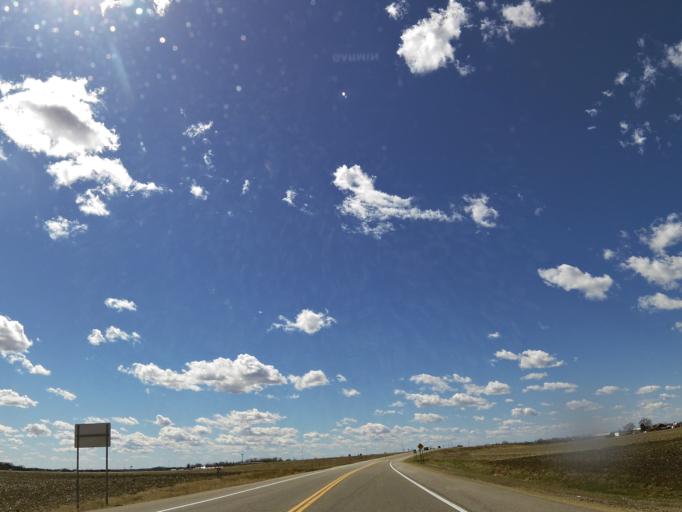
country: US
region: Minnesota
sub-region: Dakota County
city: Rosemount
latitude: 44.7129
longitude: -93.0239
